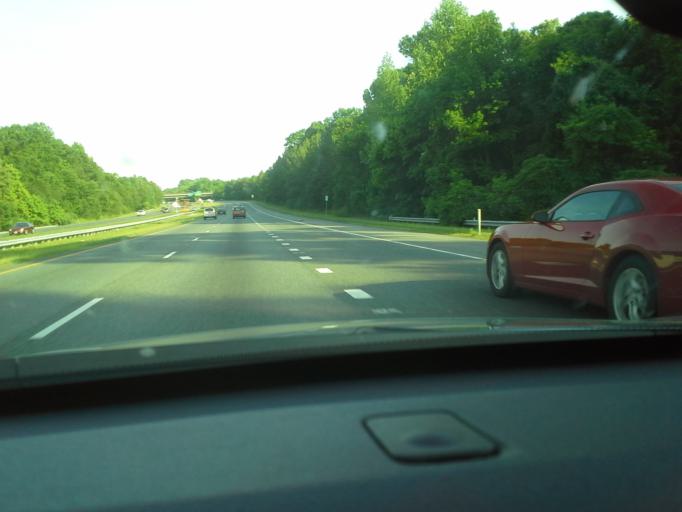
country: US
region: Maryland
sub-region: Anne Arundel County
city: Crownsville
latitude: 39.0527
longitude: -76.6279
